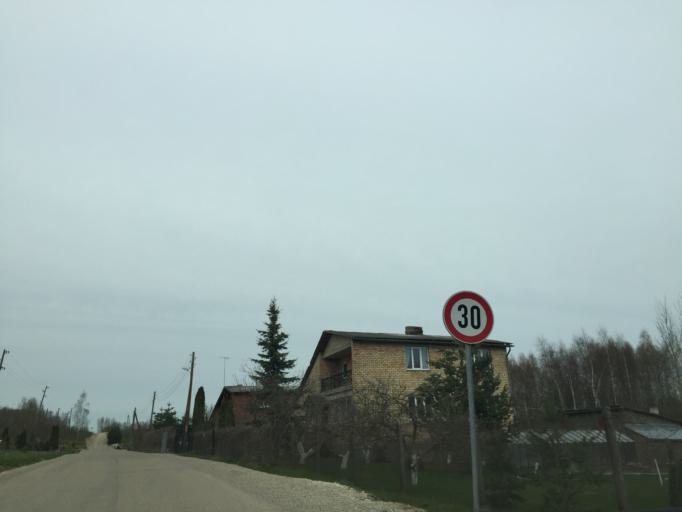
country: LV
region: Ludzas Rajons
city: Ludza
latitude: 56.5494
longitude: 27.6971
